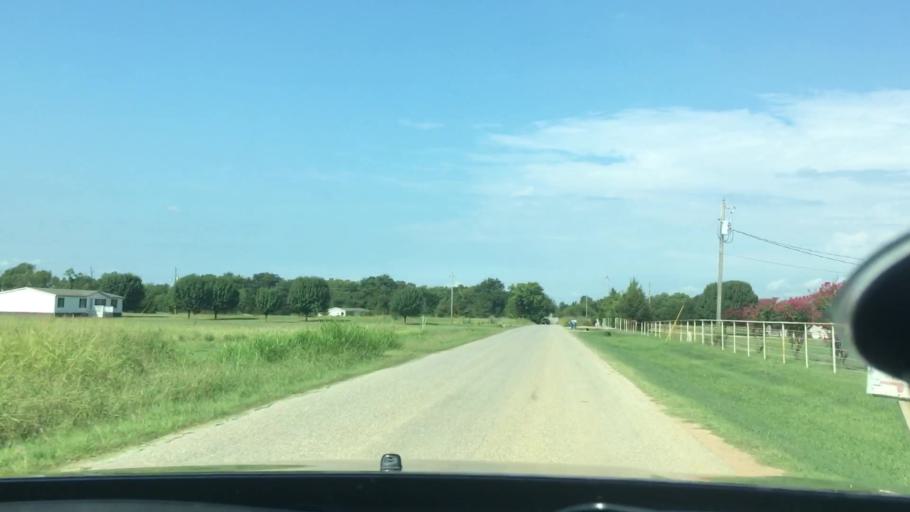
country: US
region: Oklahoma
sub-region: Bryan County
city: Calera
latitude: 33.9110
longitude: -96.4769
